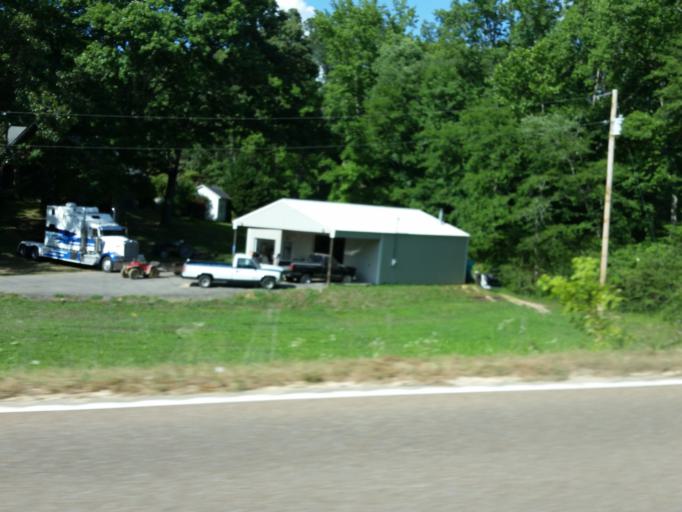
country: US
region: Tennessee
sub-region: Decatur County
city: Parsons
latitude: 35.6415
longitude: -88.0873
